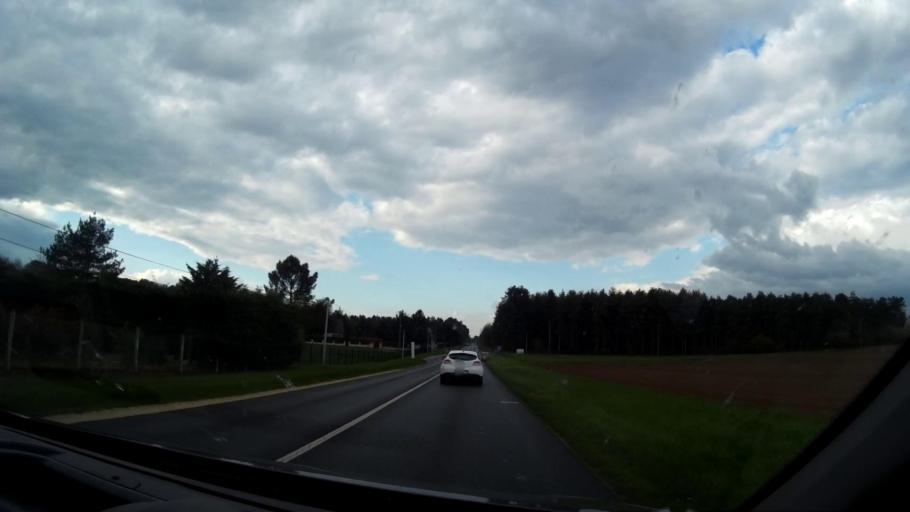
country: FR
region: Centre
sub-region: Departement du Loir-et-Cher
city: Contres
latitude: 47.4536
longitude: 1.4258
